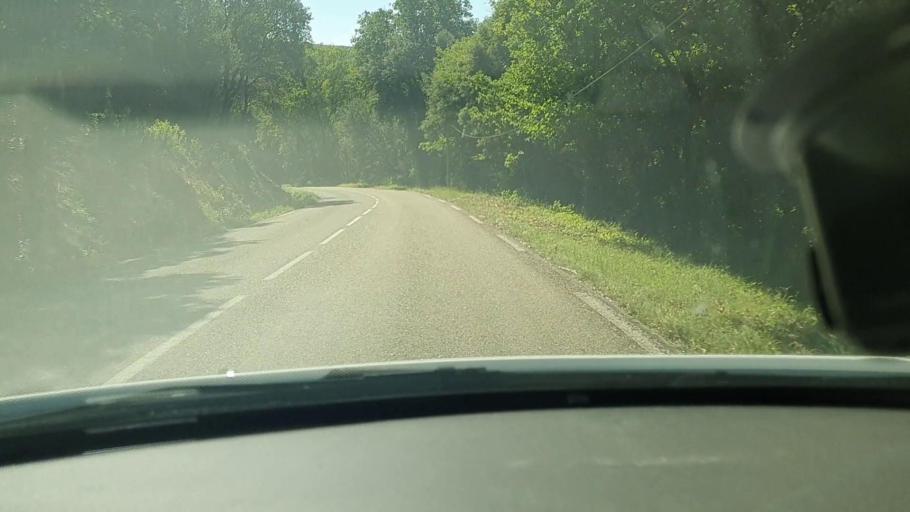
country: FR
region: Languedoc-Roussillon
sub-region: Departement du Gard
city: Saint-Paulet-de-Caisson
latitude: 44.2248
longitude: 4.5443
